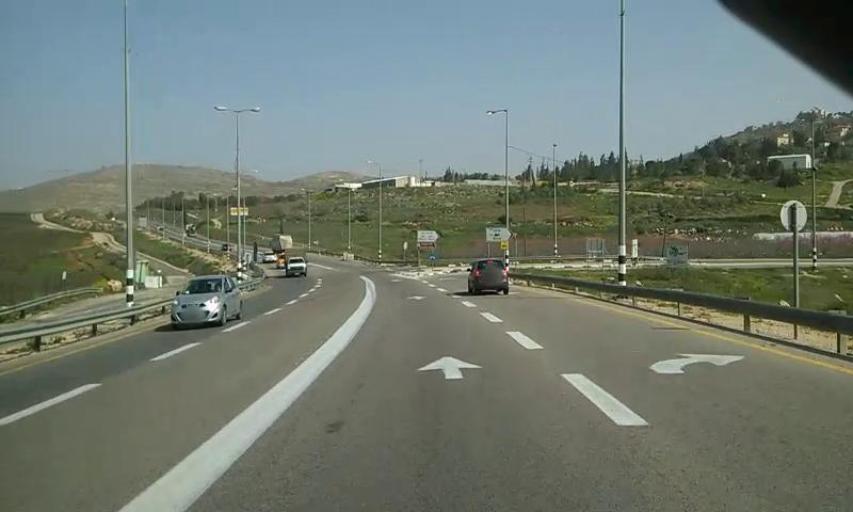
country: PS
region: West Bank
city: Turmus`ayya
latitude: 32.0530
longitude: 35.2880
